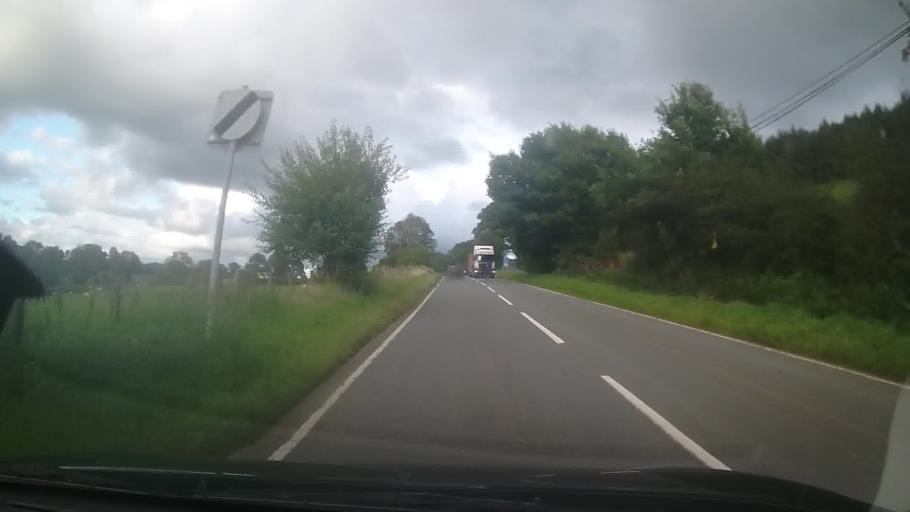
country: GB
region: Wales
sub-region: Gwynedd
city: Bala
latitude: 52.9017
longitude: -3.5869
